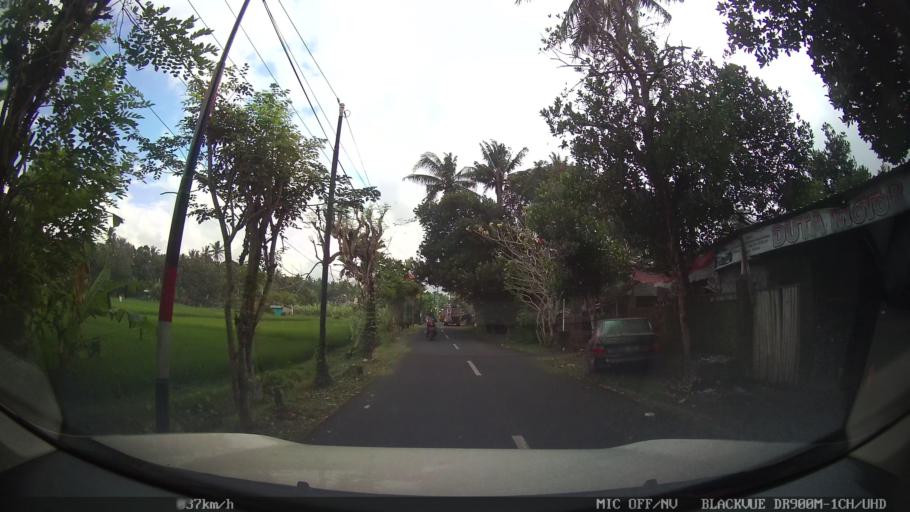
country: ID
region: Bali
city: Banjar Bucu
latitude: -8.5762
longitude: 115.2033
